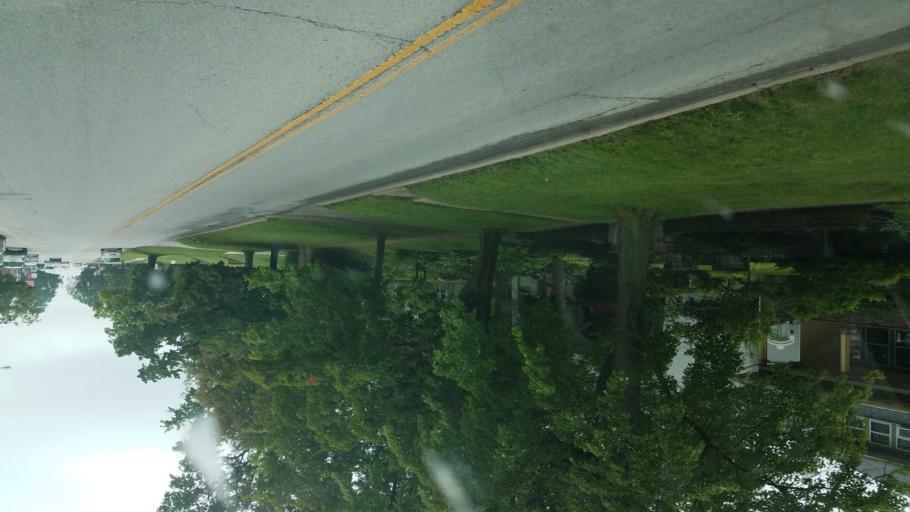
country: US
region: Ohio
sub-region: Highland County
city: Hillsboro
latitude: 39.2067
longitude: -83.6105
